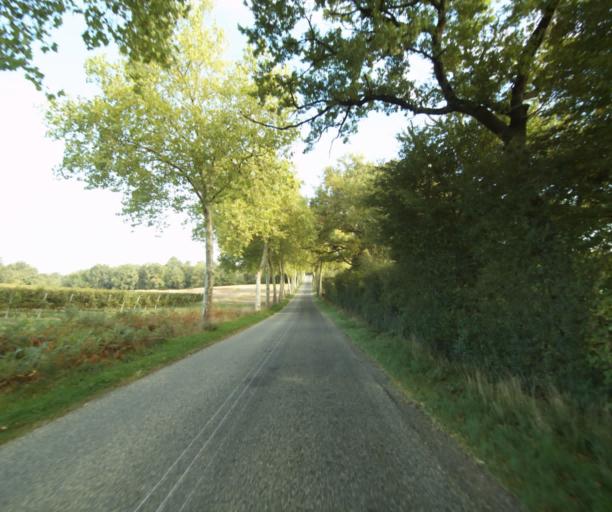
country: FR
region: Midi-Pyrenees
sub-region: Departement du Gers
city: Eauze
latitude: 43.8948
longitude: 0.0318
